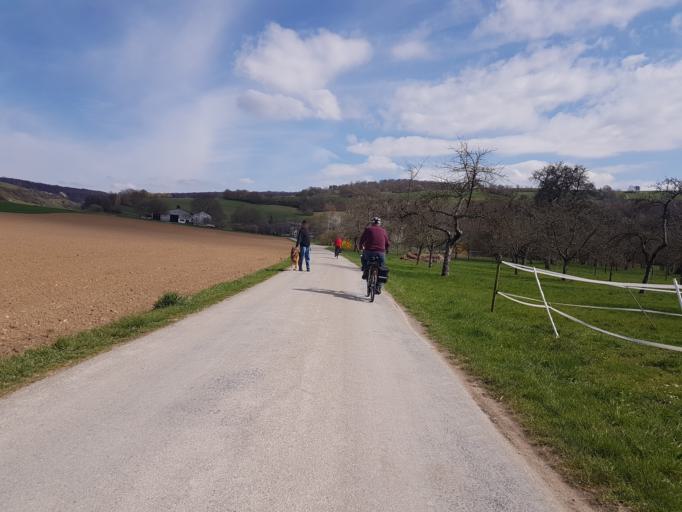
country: DE
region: Baden-Wuerttemberg
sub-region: Regierungsbezirk Stuttgart
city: Krautheim
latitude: 49.3589
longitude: 9.6096
